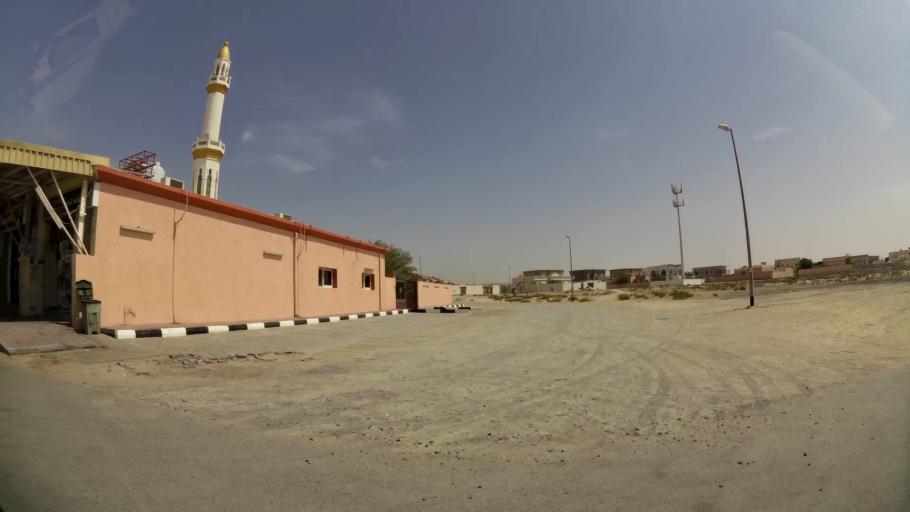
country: AE
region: Ash Shariqah
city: Sharjah
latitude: 25.1878
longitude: 55.4237
